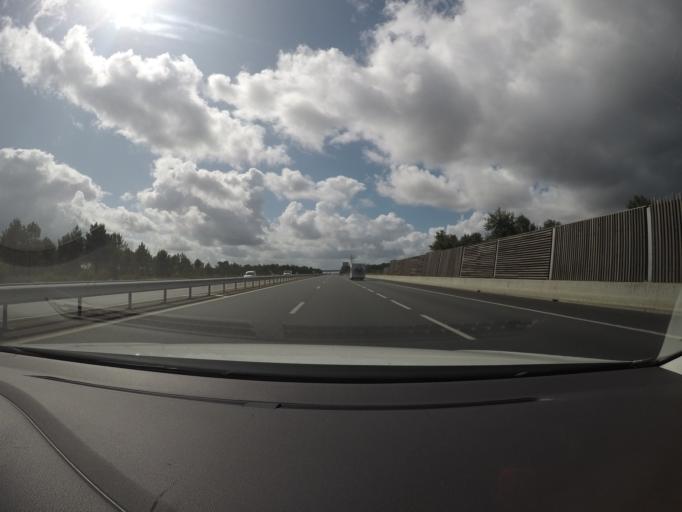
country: FR
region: Aquitaine
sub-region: Departement des Landes
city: Labouheyre
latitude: 44.2057
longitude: -0.9284
